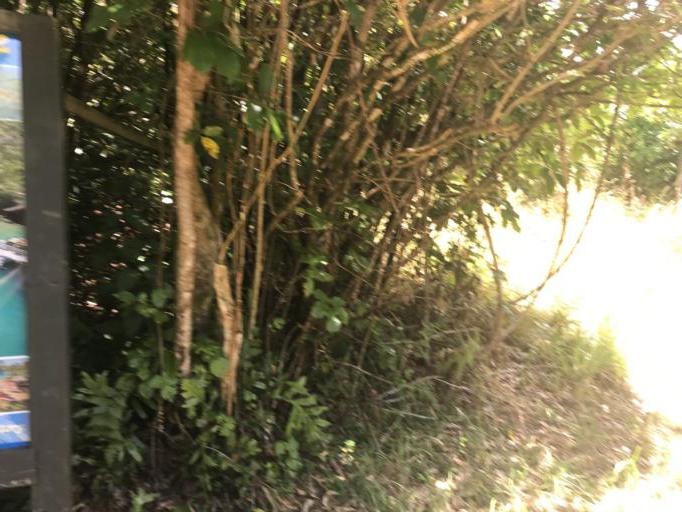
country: NZ
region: Marlborough
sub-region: Marlborough District
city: Picton
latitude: -41.2131
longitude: 173.9938
